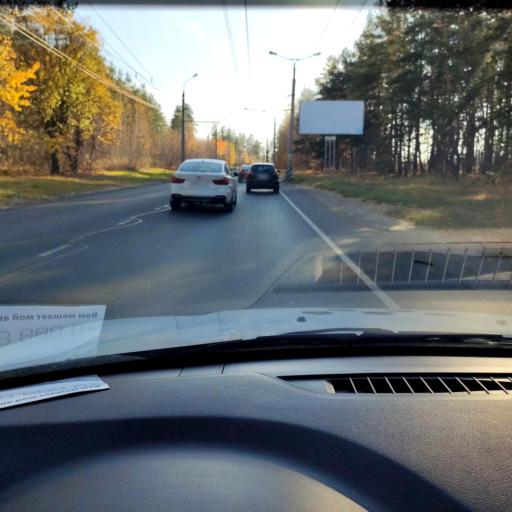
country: RU
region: Samara
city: Tol'yatti
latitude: 53.4927
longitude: 49.3859
